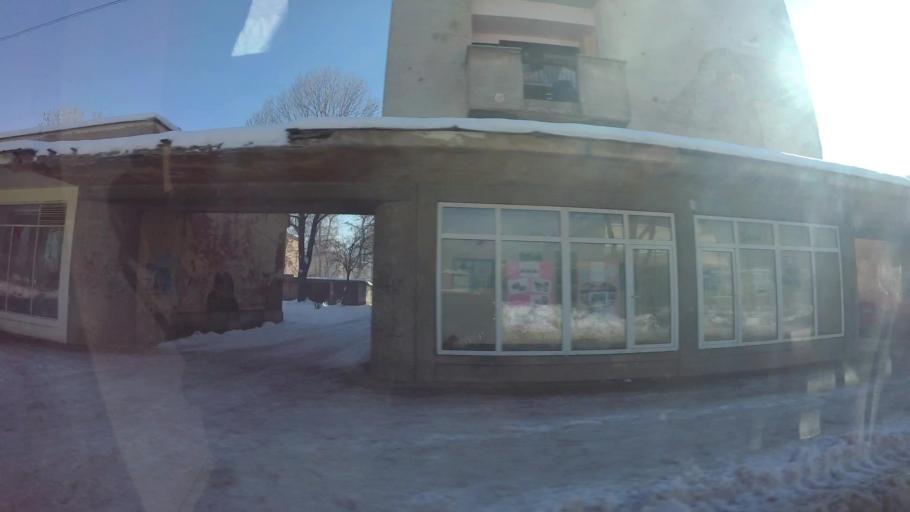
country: BA
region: Federation of Bosnia and Herzegovina
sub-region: Kanton Sarajevo
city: Sarajevo
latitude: 43.7978
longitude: 18.3144
